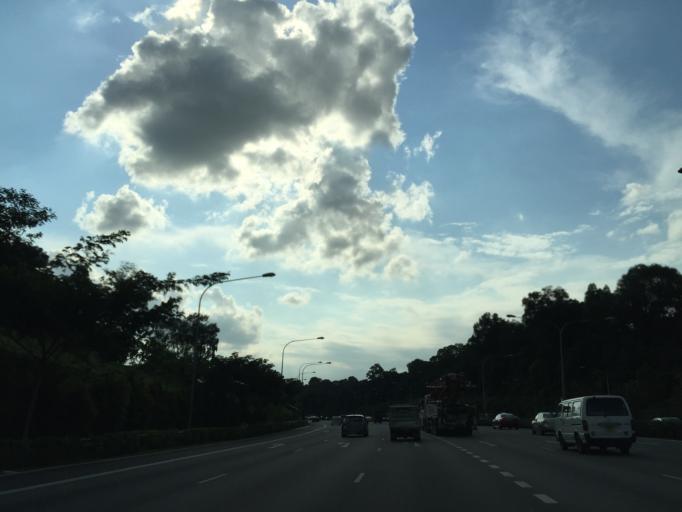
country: SG
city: Singapore
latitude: 1.3476
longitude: 103.7978
